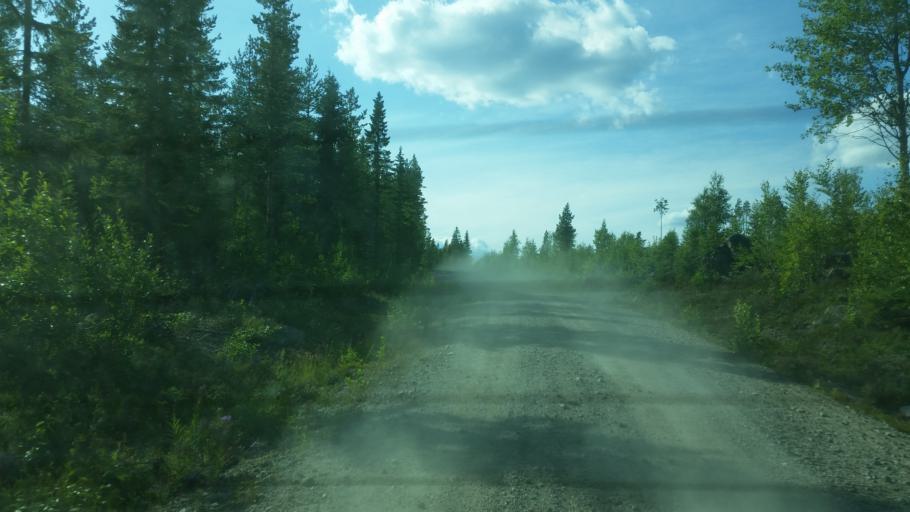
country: SE
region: Vaesternorrland
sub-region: Ange Kommun
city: Ange
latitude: 62.2716
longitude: 15.4000
